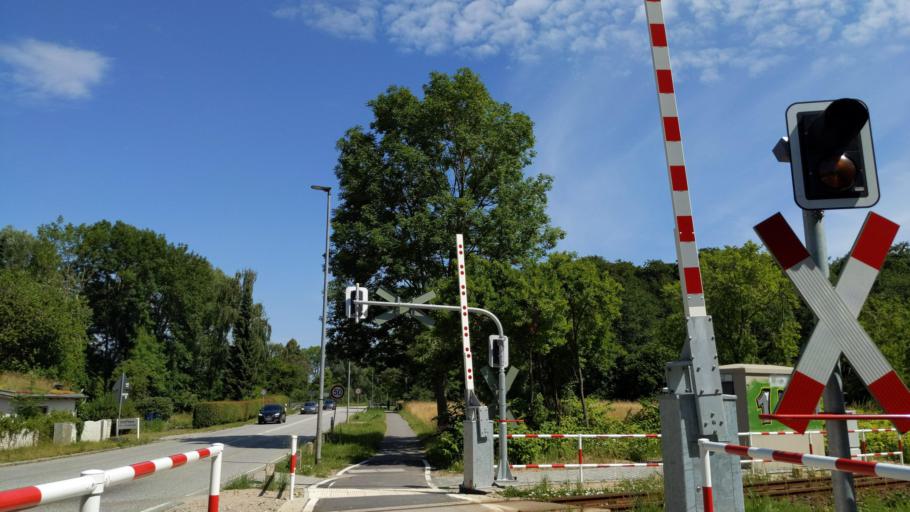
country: DE
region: Schleswig-Holstein
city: Ploen
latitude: 54.1495
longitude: 10.4011
